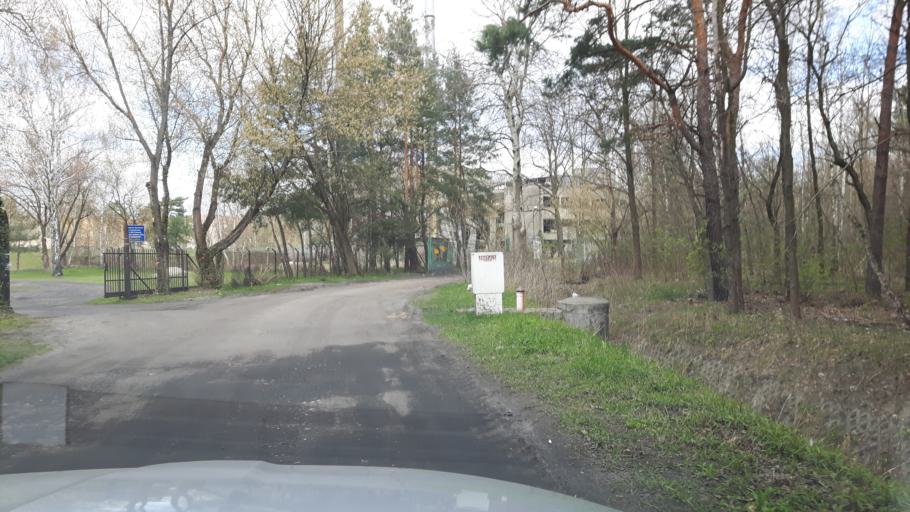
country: PL
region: Masovian Voivodeship
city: Zielonka
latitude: 52.2988
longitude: 21.1666
